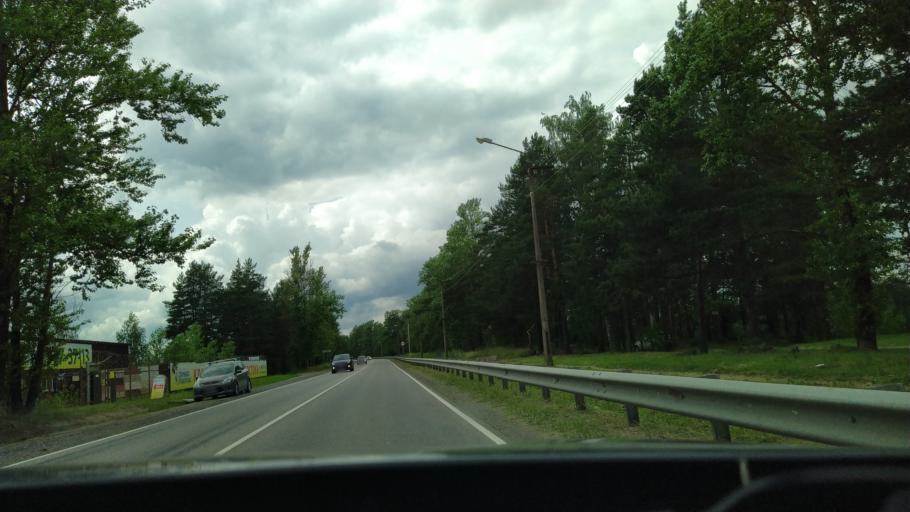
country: RU
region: Leningrad
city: Pavlovo
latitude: 59.8086
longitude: 30.8717
